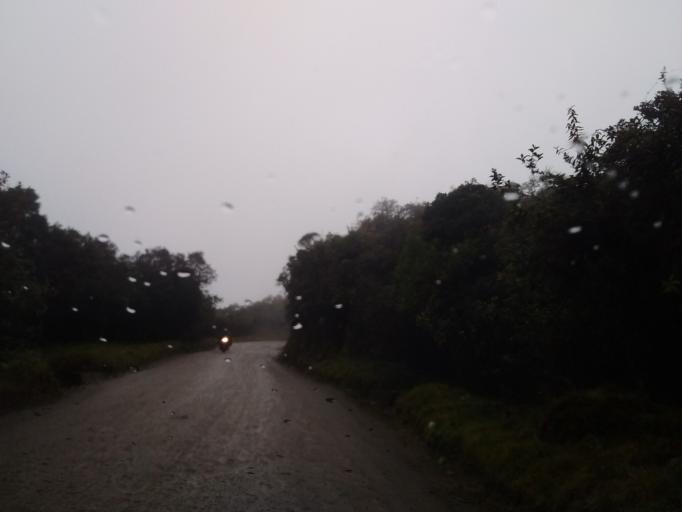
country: CO
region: Cauca
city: Paispamba
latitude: 2.1539
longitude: -76.4181
